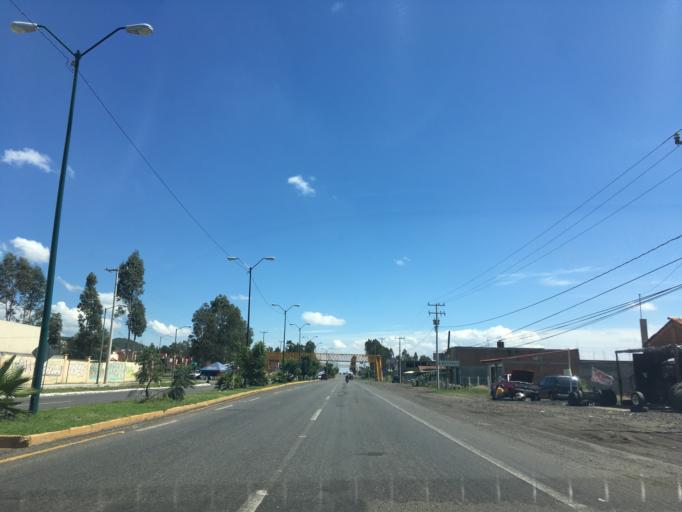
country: MX
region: Michoacan
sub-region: Morelia
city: Lomas de la Maestranza
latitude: 19.6839
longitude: -101.3332
